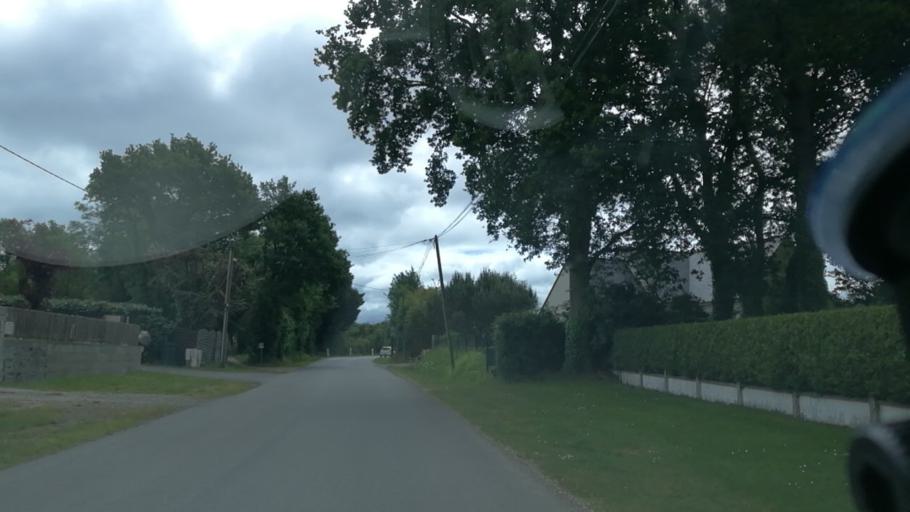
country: FR
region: Brittany
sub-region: Departement du Morbihan
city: Penestin
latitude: 47.4904
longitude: -2.4372
